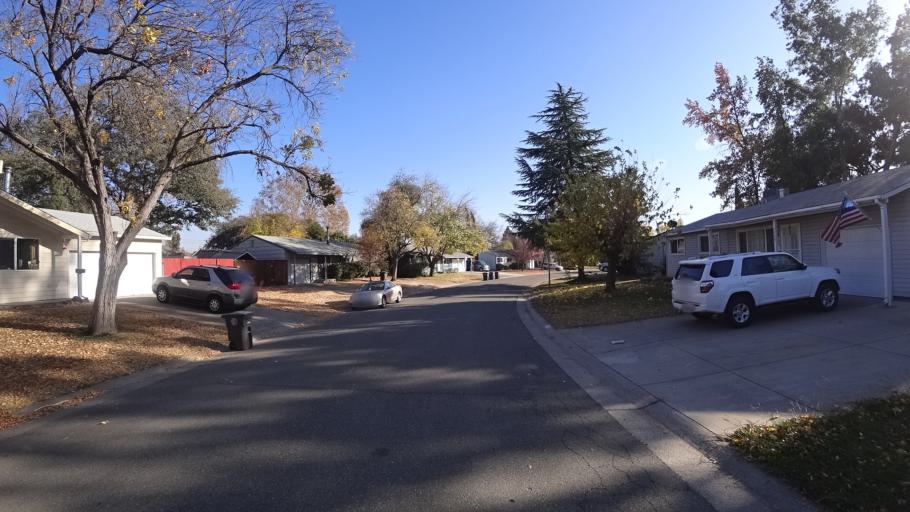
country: US
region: California
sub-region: Sacramento County
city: Antelope
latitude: 38.7028
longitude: -121.3125
